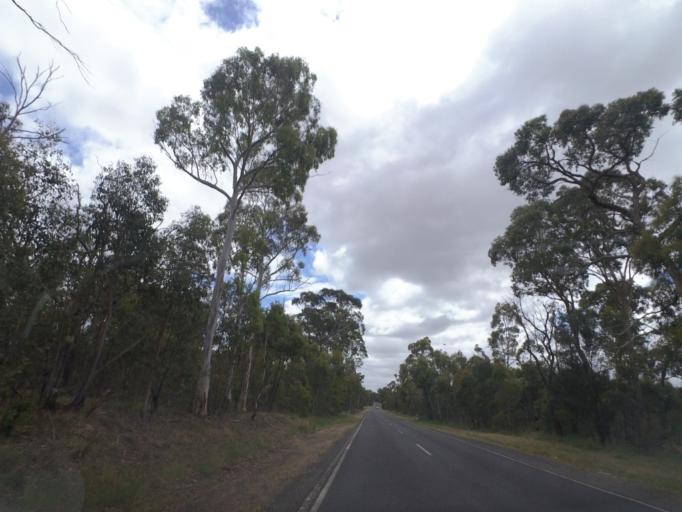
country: AU
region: Victoria
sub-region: Whittlesea
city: Whittlesea
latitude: -37.2953
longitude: 145.0573
